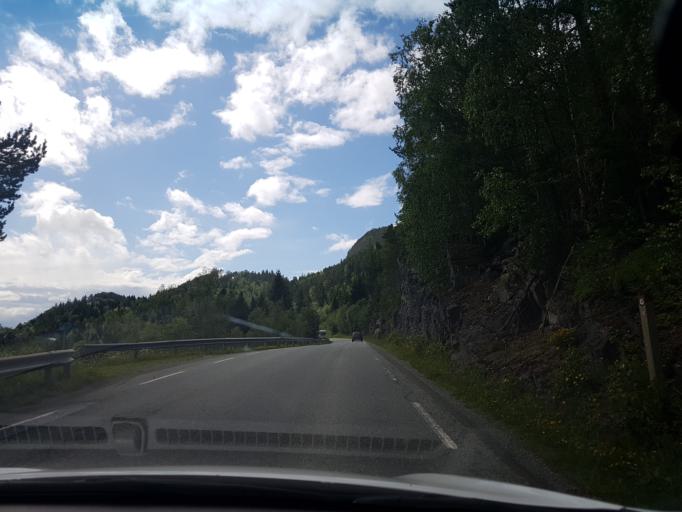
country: NO
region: Nord-Trondelag
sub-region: Frosta
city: Frosta
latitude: 63.6076
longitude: 10.8843
